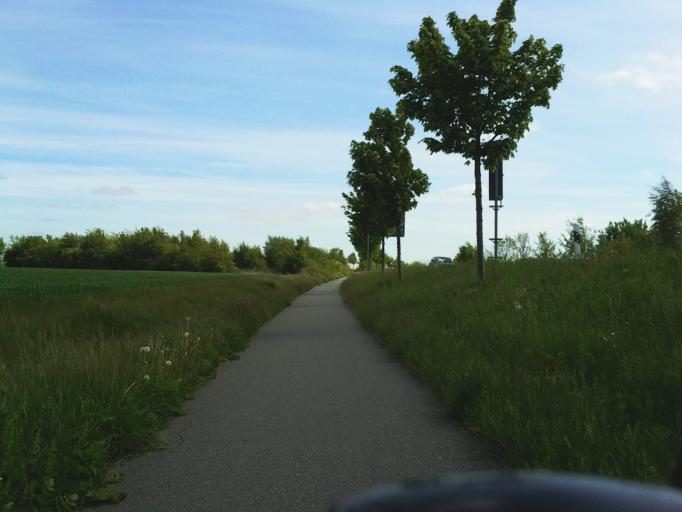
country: DE
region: Mecklenburg-Vorpommern
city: Papendorf
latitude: 54.0548
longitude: 12.1183
